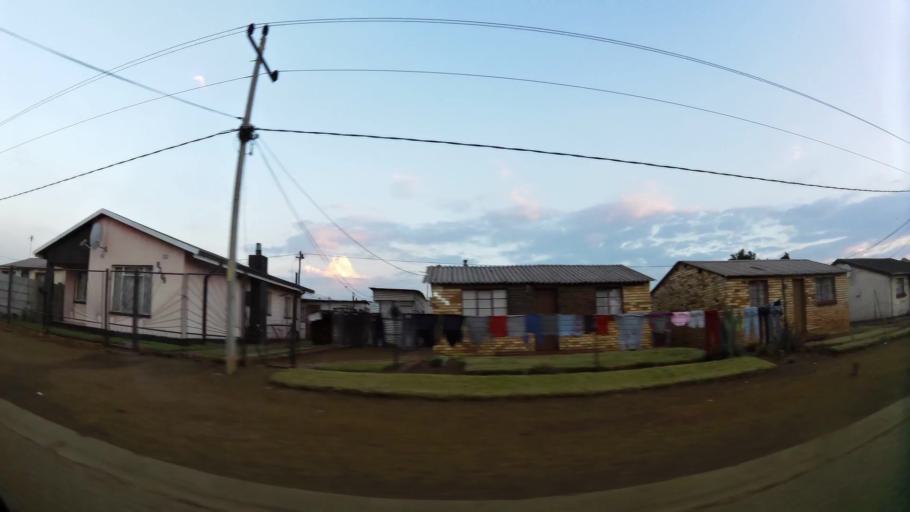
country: ZA
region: Gauteng
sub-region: City of Johannesburg Metropolitan Municipality
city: Orange Farm
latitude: -26.5518
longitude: 27.8793
